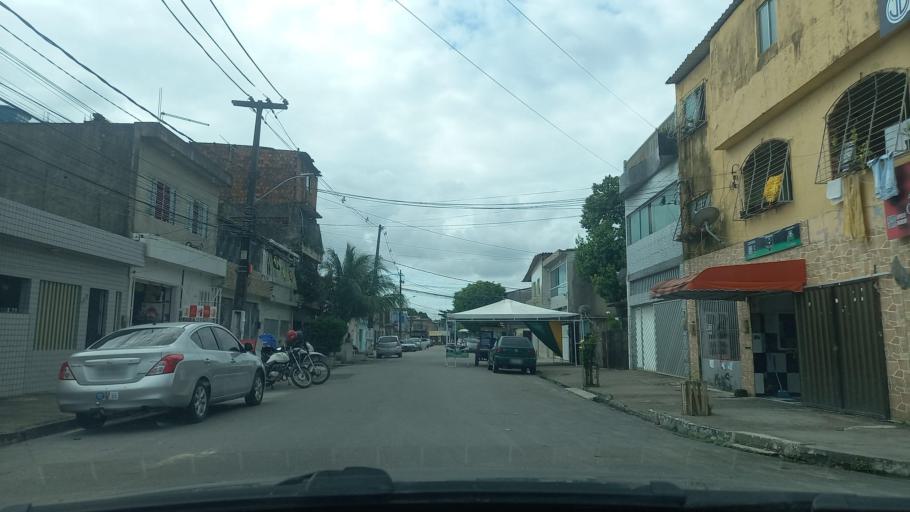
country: BR
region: Pernambuco
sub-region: Recife
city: Recife
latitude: -8.1058
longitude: -34.9178
